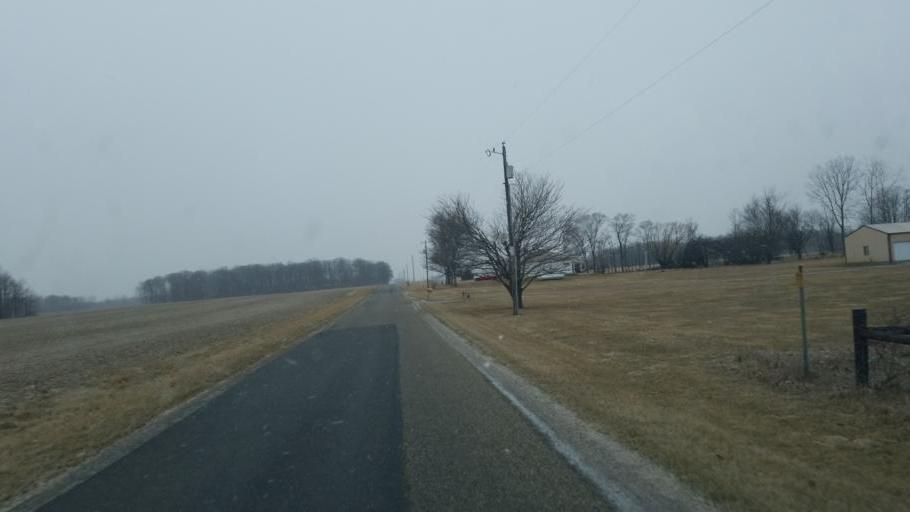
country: US
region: Ohio
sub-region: Defiance County
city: Hicksville
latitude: 41.3393
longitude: -84.7312
